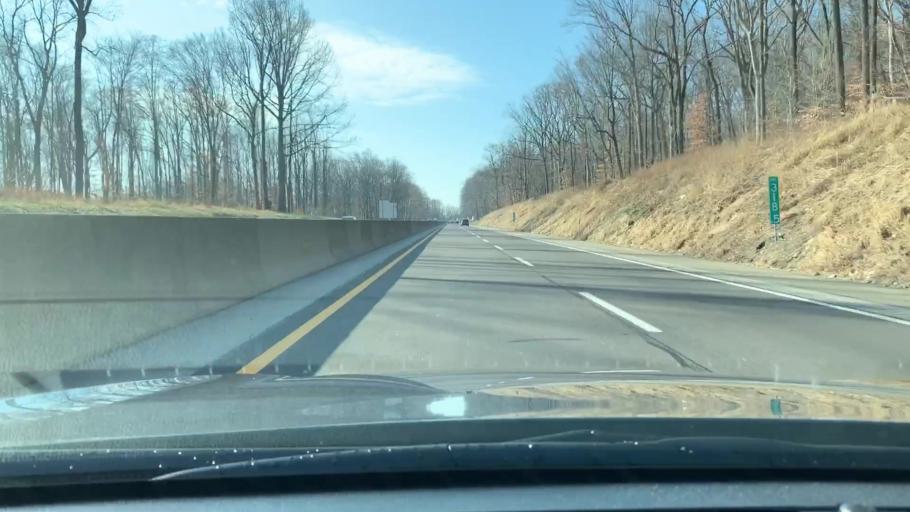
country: US
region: Pennsylvania
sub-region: Chester County
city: Malvern
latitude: 40.0752
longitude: -75.5520
